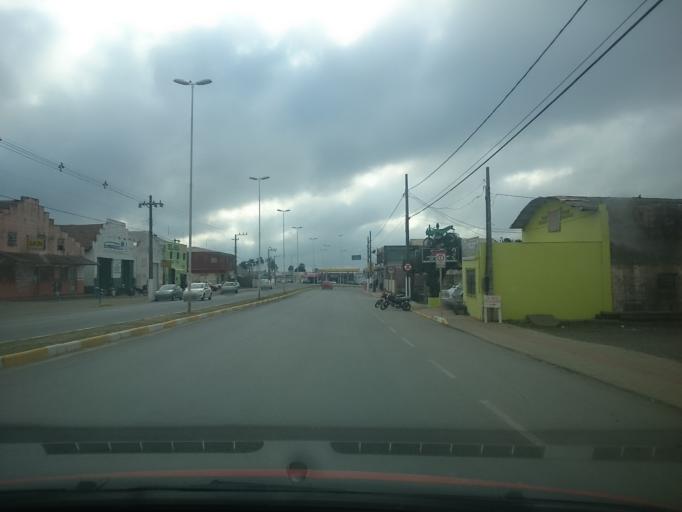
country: BR
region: Santa Catarina
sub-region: Lages
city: Lages
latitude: -27.8294
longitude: -50.3395
